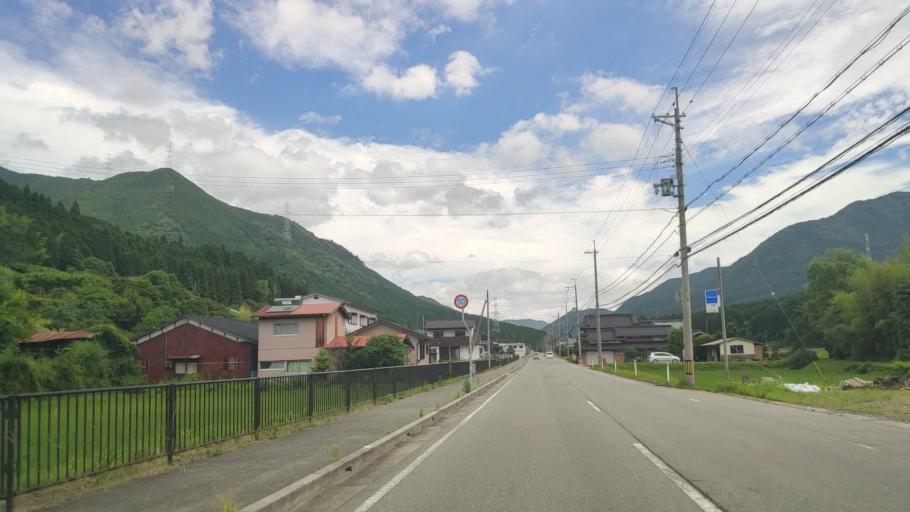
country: JP
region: Hyogo
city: Nishiwaki
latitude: 35.1494
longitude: 134.9248
